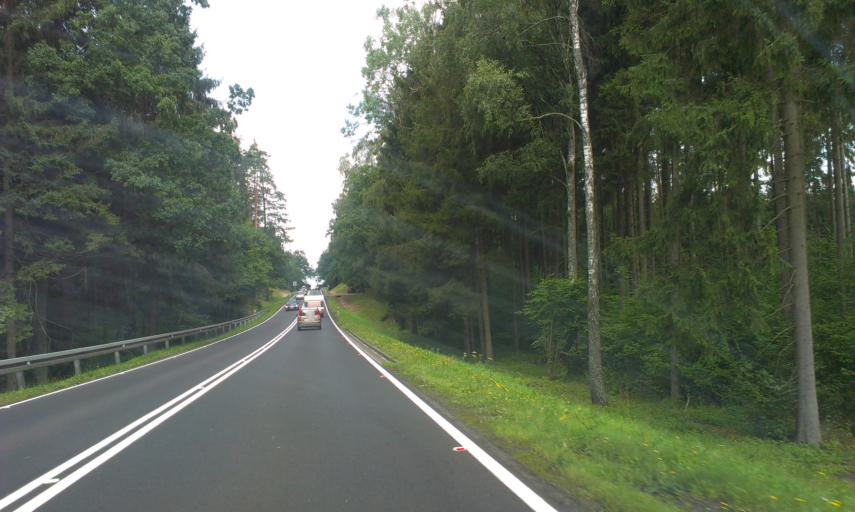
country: PL
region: West Pomeranian Voivodeship
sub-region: Powiat koszalinski
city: Bobolice
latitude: 53.9955
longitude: 16.5287
